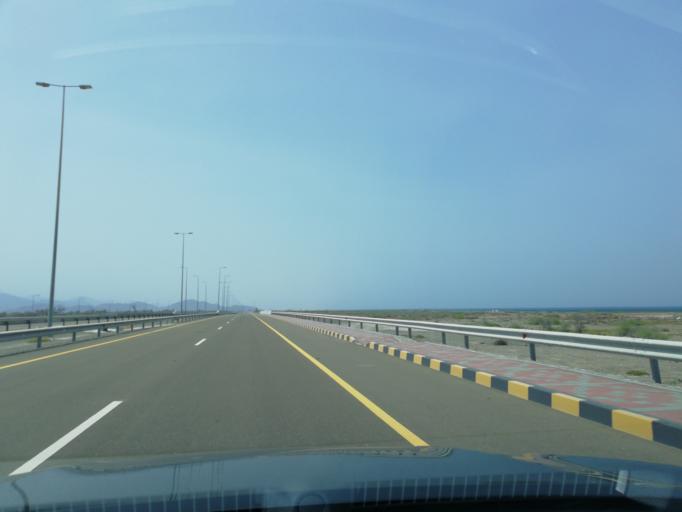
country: OM
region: Al Batinah
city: Shinas
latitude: 24.8955
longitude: 56.3990
